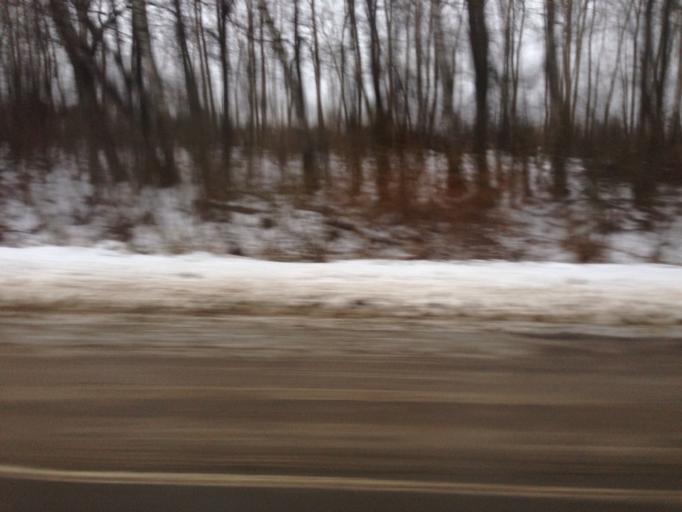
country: RU
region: Tula
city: Partizan
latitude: 54.0094
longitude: 38.0977
